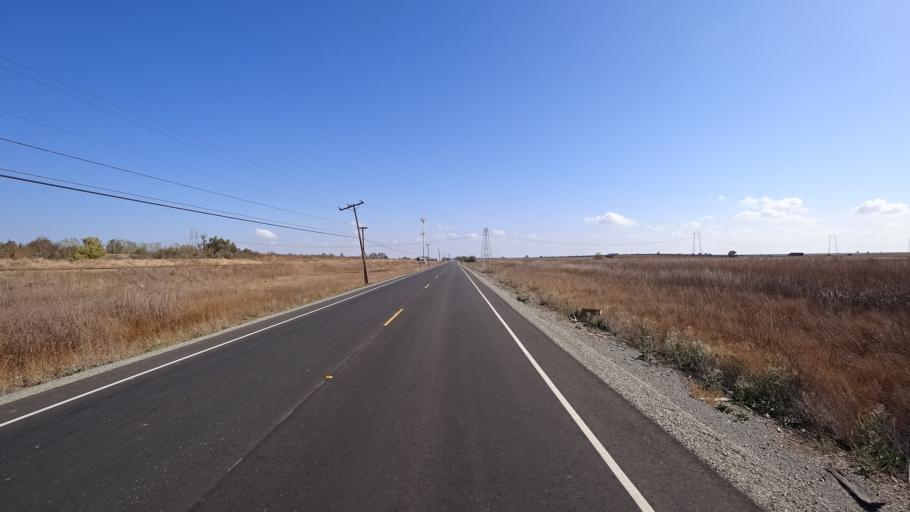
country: US
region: California
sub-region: Yolo County
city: Woodland
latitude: 38.6767
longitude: -121.6805
